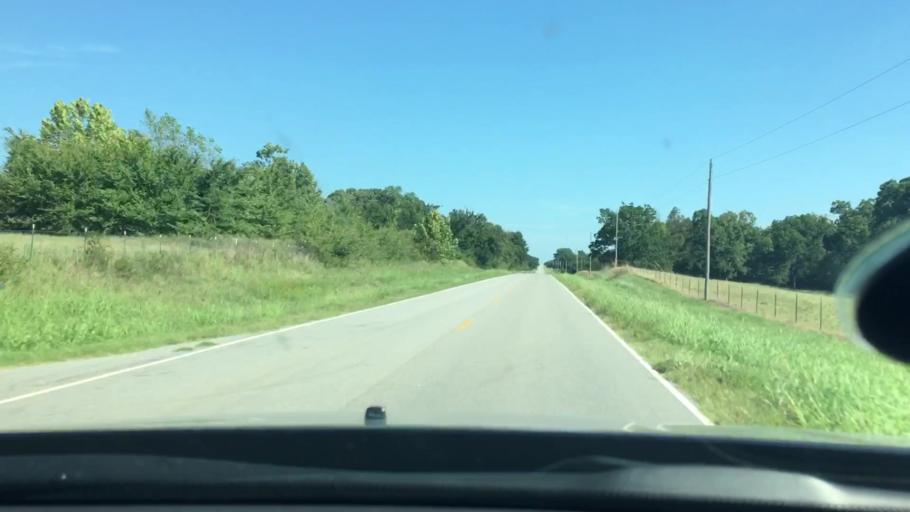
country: US
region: Oklahoma
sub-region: Johnston County
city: Tishomingo
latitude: 34.2856
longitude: -96.5487
